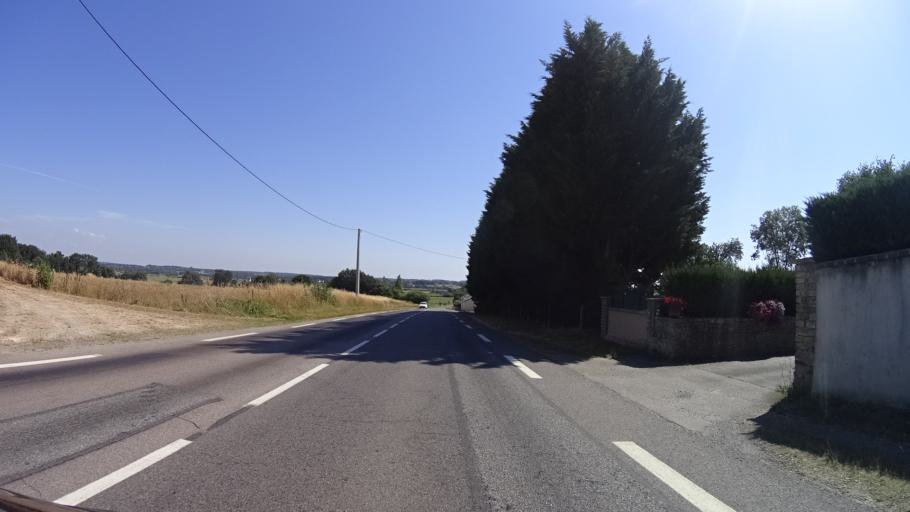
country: FR
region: Brittany
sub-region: Departement du Morbihan
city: Rieux
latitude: 47.5873
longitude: -2.1103
